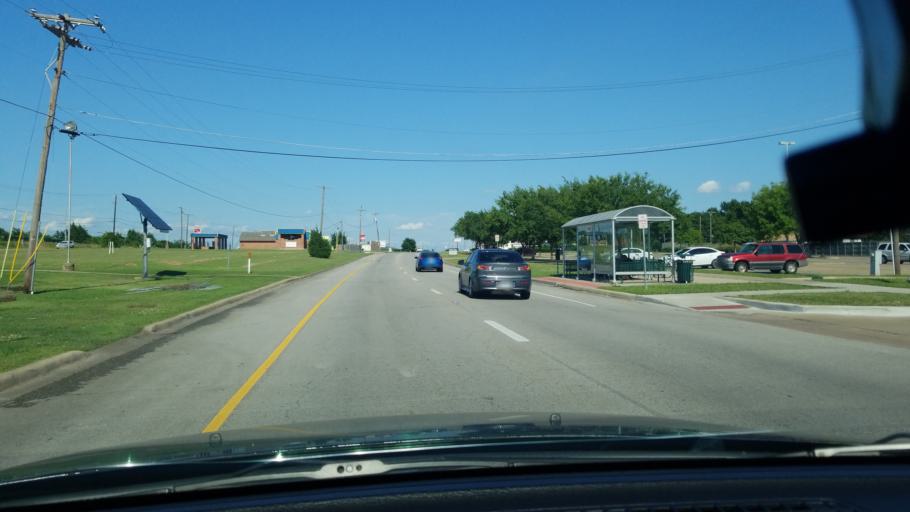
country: US
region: Texas
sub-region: Dallas County
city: Mesquite
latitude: 32.7659
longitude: -96.5911
